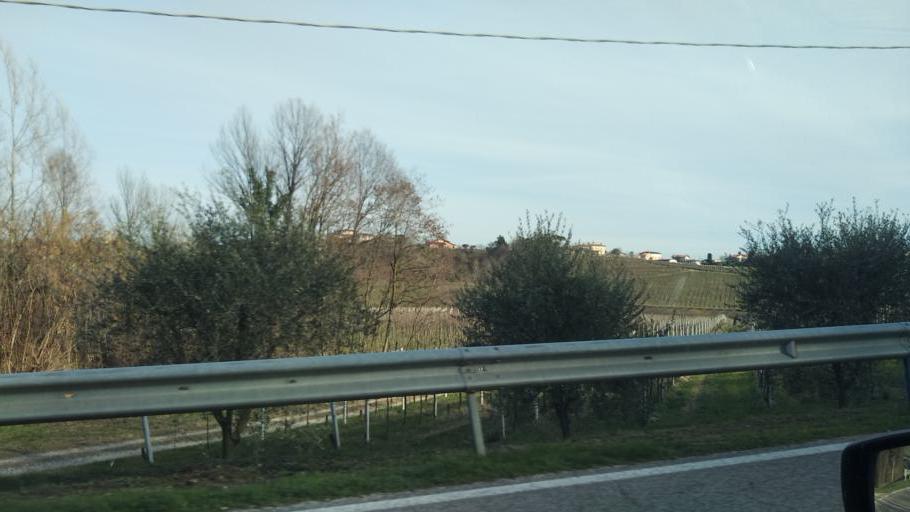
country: IT
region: Veneto
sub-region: Provincia di Treviso
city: Carpesica
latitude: 45.9582
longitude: 12.2830
